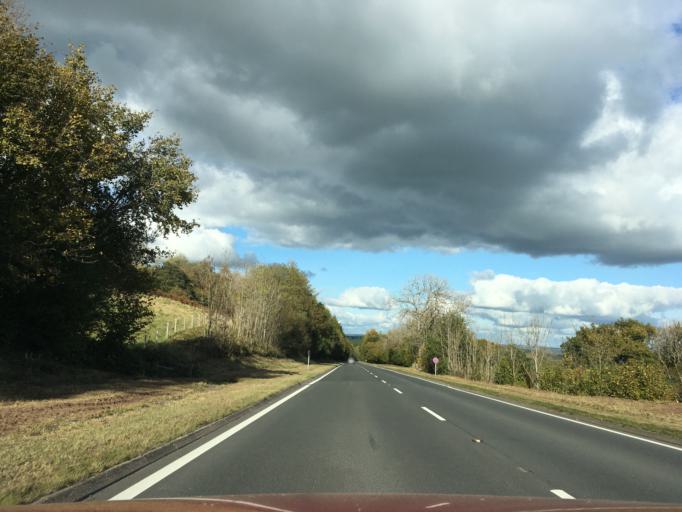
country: GB
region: Wales
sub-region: Sir Powys
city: Brecon
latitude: 51.8956
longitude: -3.4935
